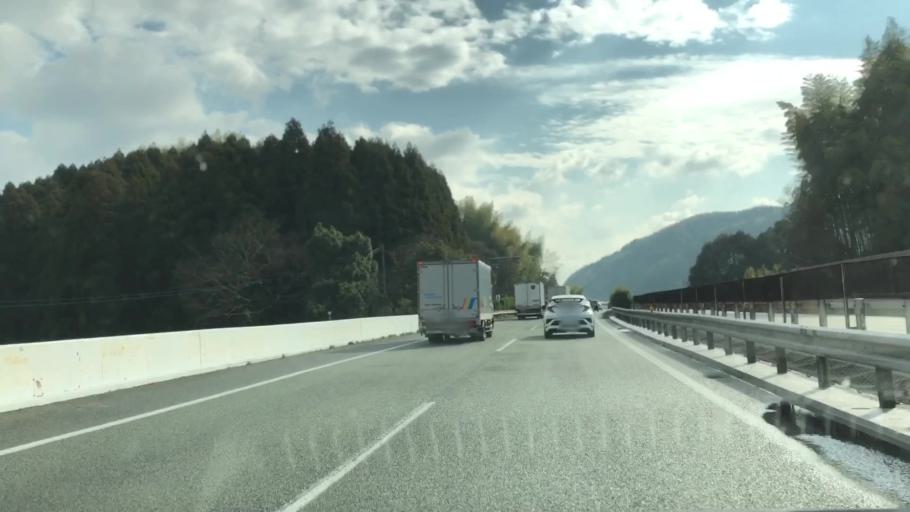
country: JP
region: Fukuoka
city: Setakamachi-takayanagi
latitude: 33.1061
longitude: 130.5341
